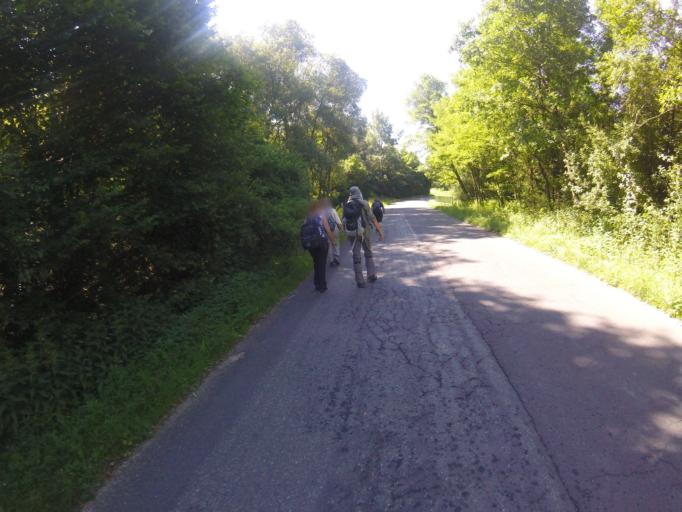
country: HU
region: Zala
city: Zalalovo
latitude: 46.8456
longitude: 16.5028
